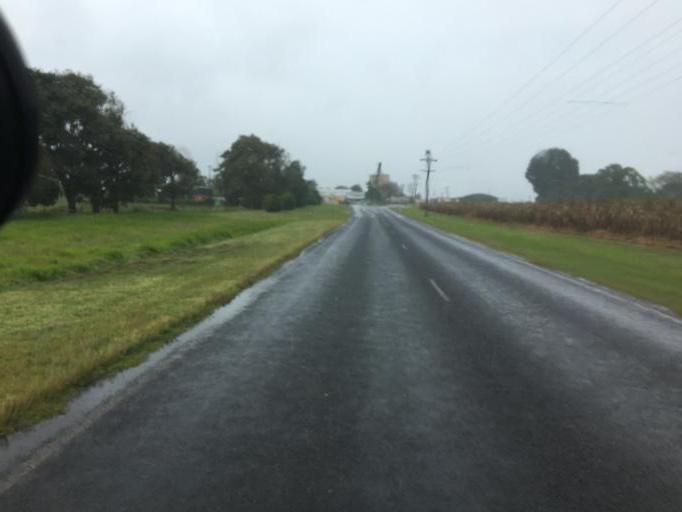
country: AU
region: Queensland
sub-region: Tablelands
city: Tolga
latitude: -17.2159
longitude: 145.5361
